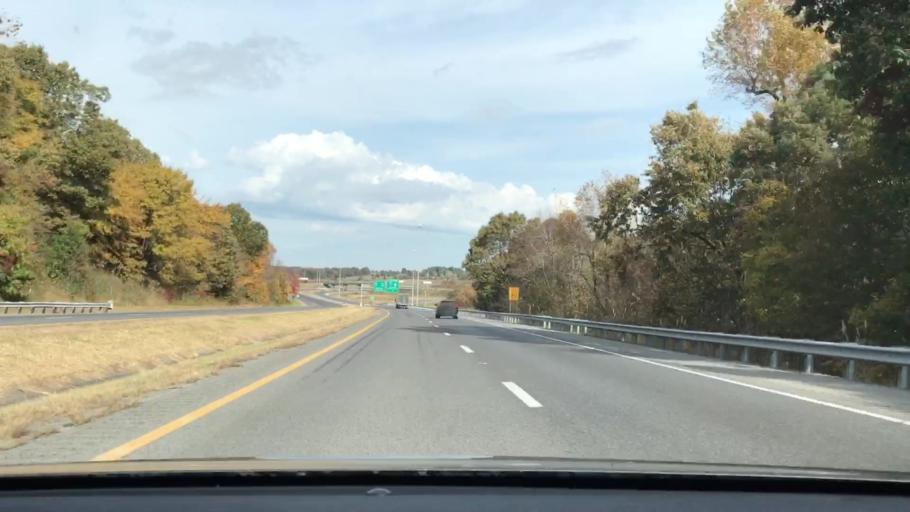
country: US
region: Kentucky
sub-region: Marshall County
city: Calvert City
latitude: 36.9765
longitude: -88.3457
